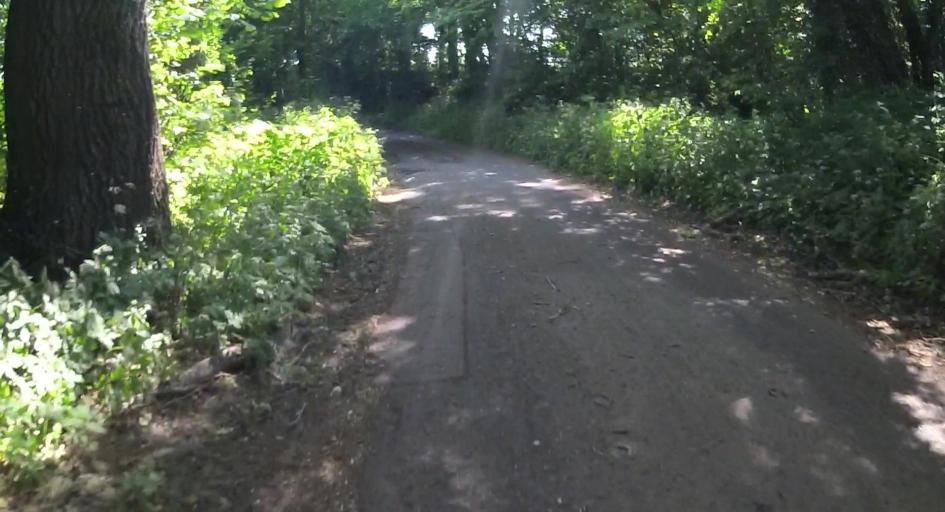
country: GB
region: England
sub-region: Hampshire
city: Kingsclere
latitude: 51.3573
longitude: -1.2760
